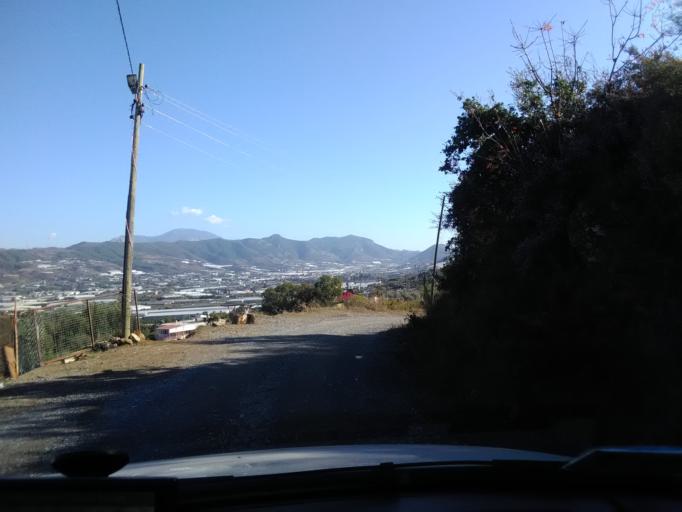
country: TR
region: Antalya
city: Gazipasa
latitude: 36.2506
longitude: 32.3332
